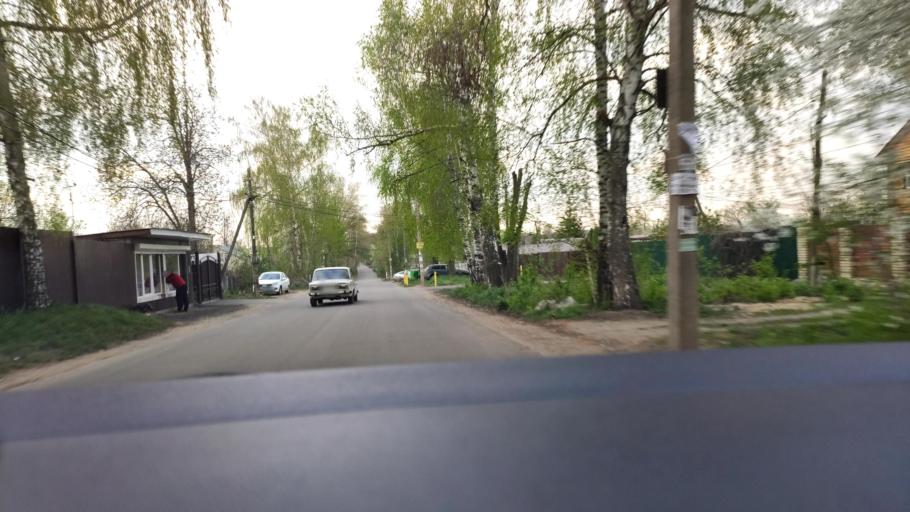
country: RU
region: Voronezj
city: Voronezh
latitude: 51.6041
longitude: 39.1581
